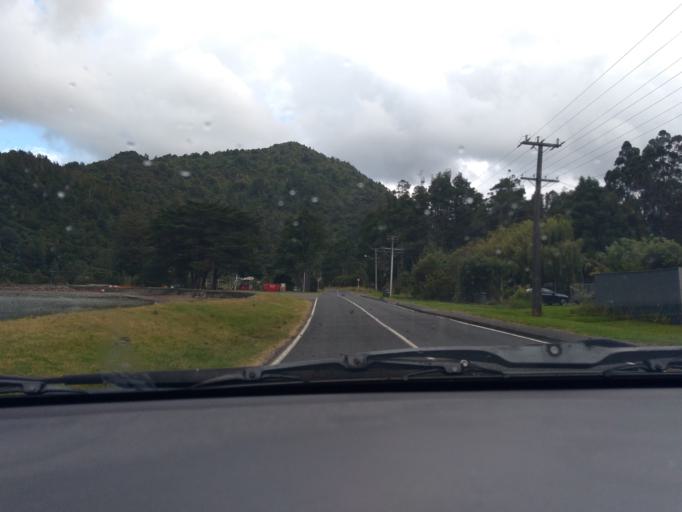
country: NZ
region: Auckland
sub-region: Auckland
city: Titirangi
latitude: -37.0000
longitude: 174.5716
